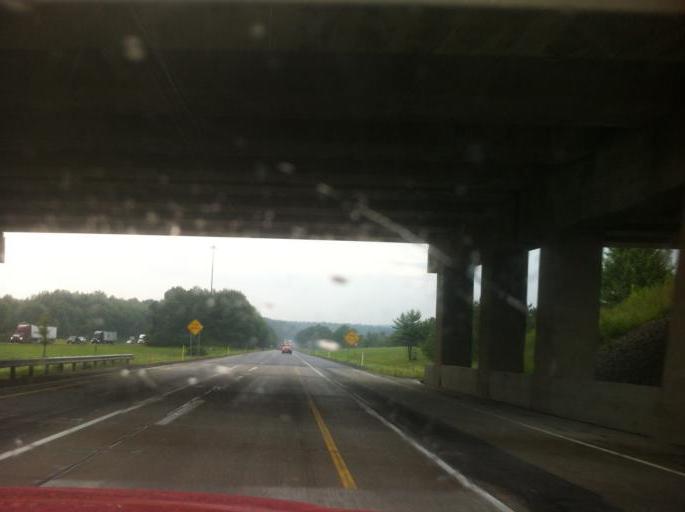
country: US
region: Pennsylvania
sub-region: Clarion County
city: Clarion
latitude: 41.1861
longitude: -79.3938
